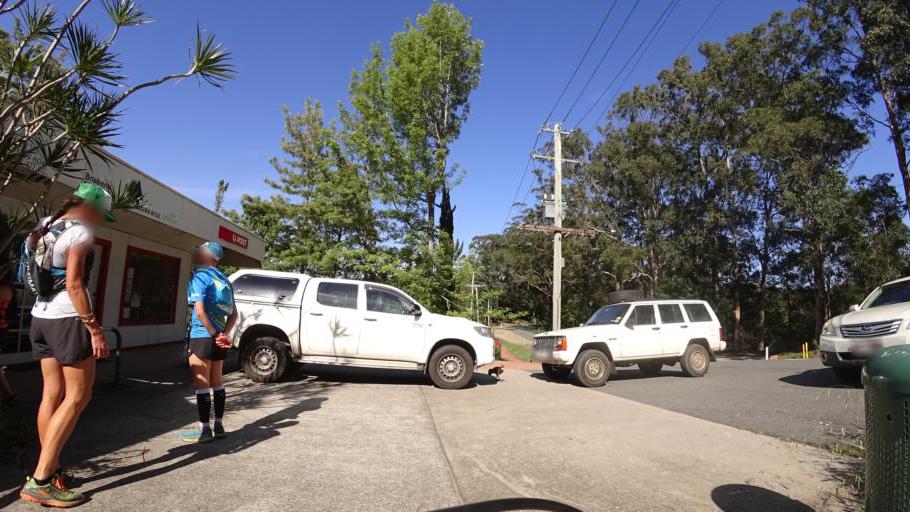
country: AU
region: Queensland
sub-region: Moreton Bay
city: Highvale
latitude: -27.3990
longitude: 152.7888
